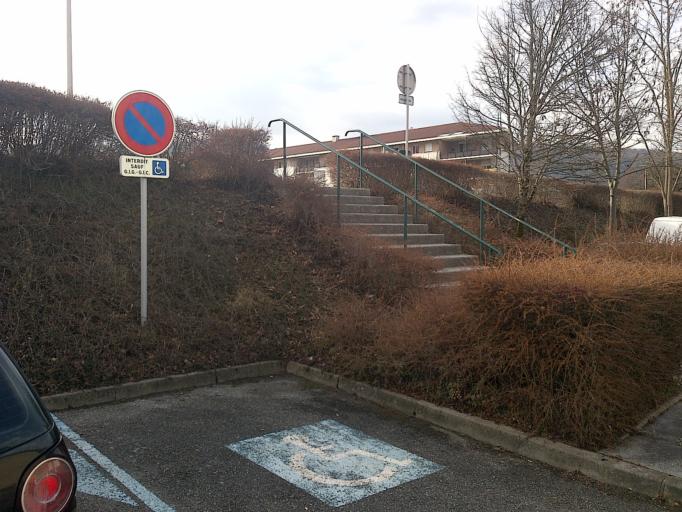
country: FR
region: Rhone-Alpes
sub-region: Departement de l'Isere
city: Eybens
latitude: 45.1475
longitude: 5.7458
